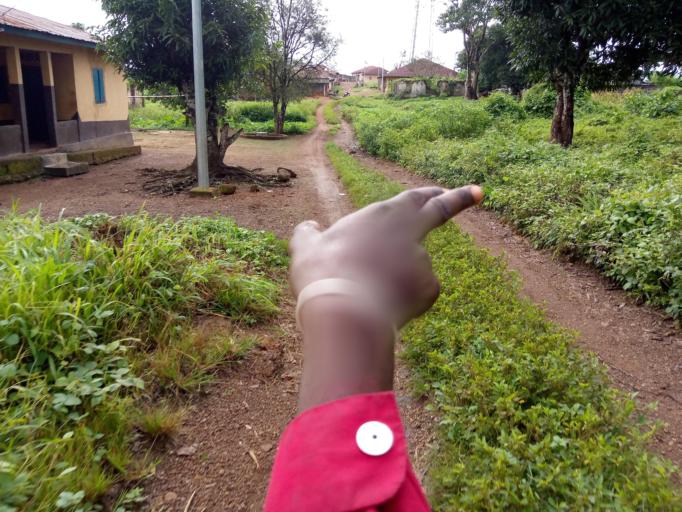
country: SL
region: Eastern Province
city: Buedu
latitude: 8.4625
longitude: -10.3407
